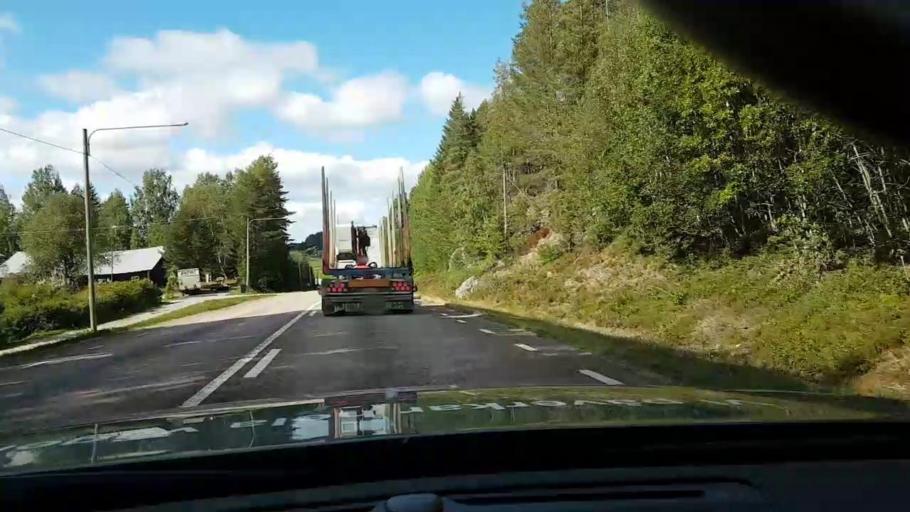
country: SE
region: Vaesternorrland
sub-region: OErnskoeldsviks Kommun
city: Bjasta
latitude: 63.3839
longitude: 18.3957
